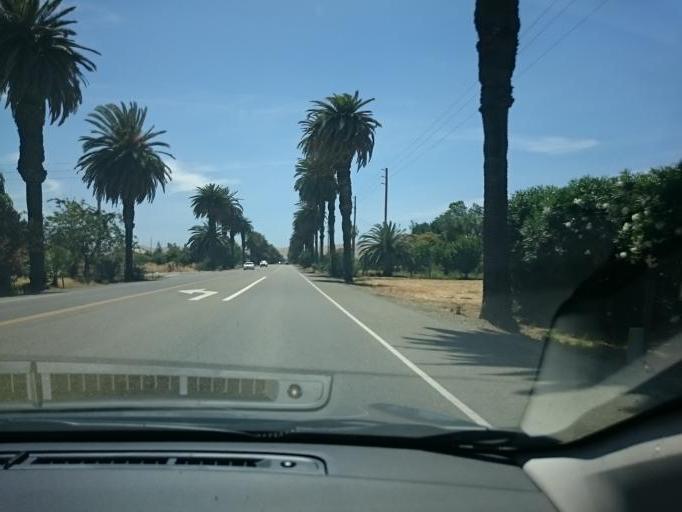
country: US
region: California
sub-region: Stanislaus County
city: Patterson
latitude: 37.4835
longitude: -121.1042
